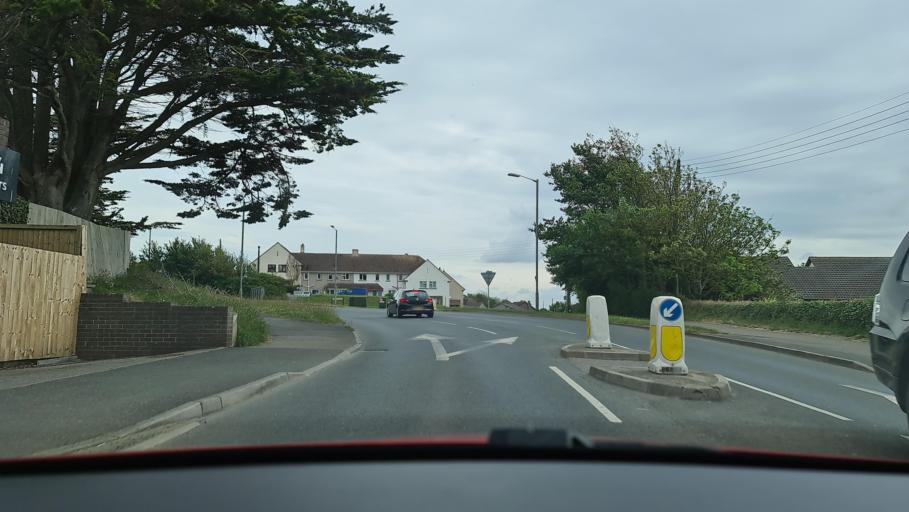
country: GB
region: England
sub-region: Cornwall
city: Bude
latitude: 50.8249
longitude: -4.5414
